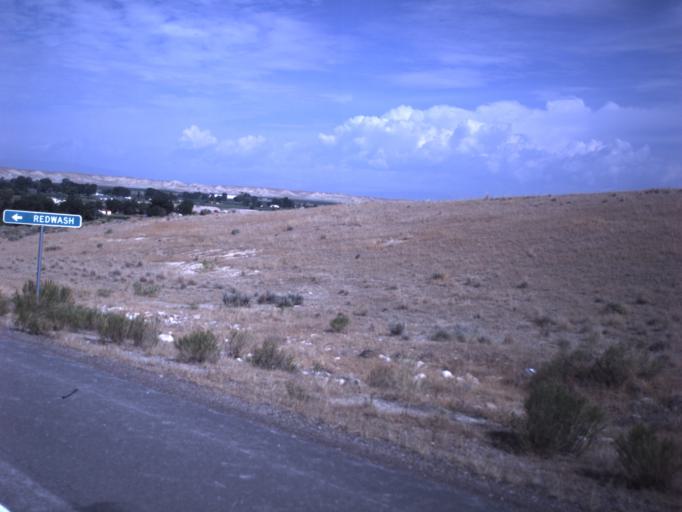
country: US
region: Utah
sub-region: Uintah County
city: Naples
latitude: 40.3695
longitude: -109.3293
